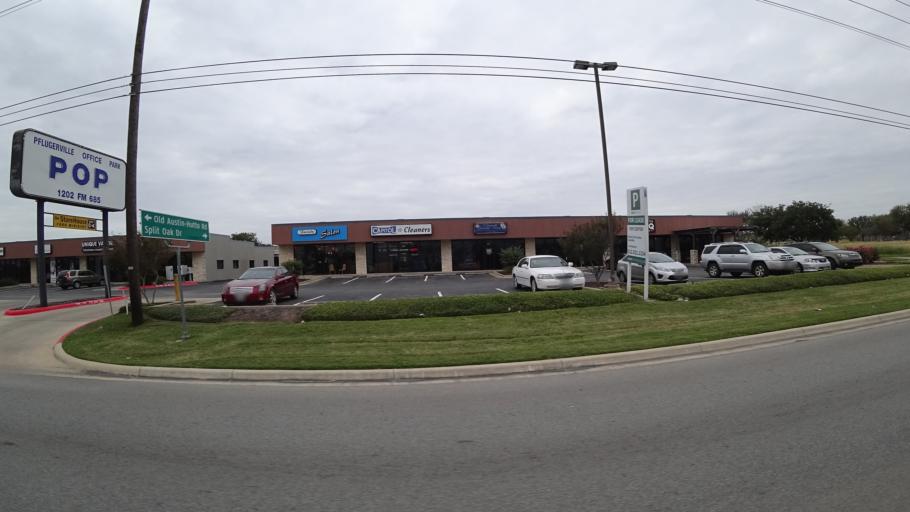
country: US
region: Texas
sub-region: Travis County
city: Pflugerville
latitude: 30.4469
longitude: -97.6074
